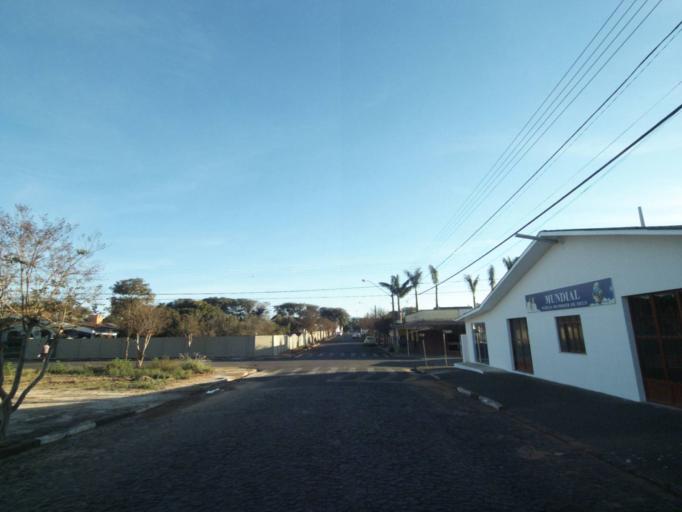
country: BR
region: Parana
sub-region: Tibagi
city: Tibagi
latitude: -24.5158
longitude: -50.4130
